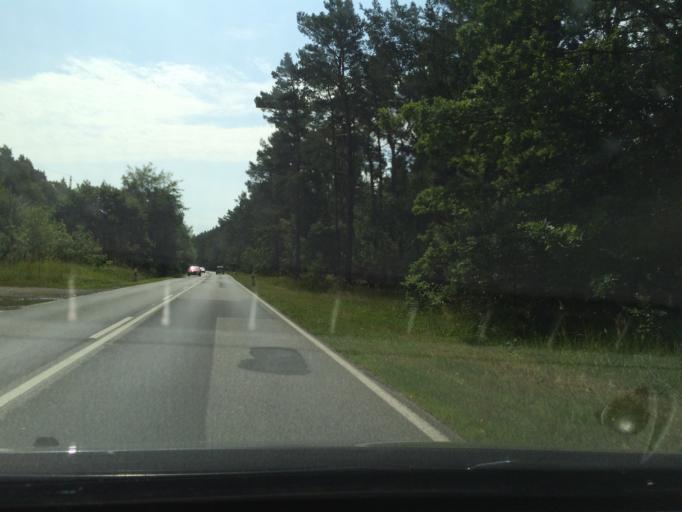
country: DE
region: Mecklenburg-Vorpommern
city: Ostseebad Binz
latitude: 54.4300
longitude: 13.5743
